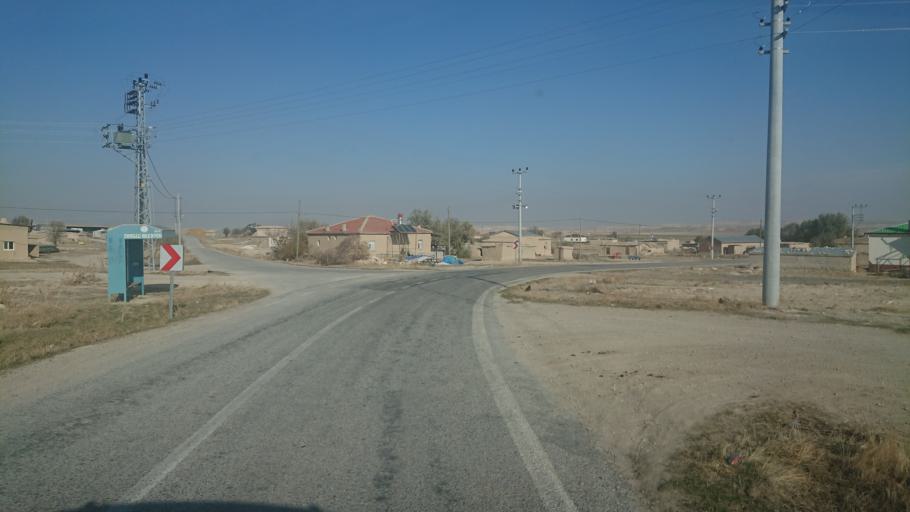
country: TR
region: Aksaray
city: Sultanhani
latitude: 38.0399
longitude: 33.5923
